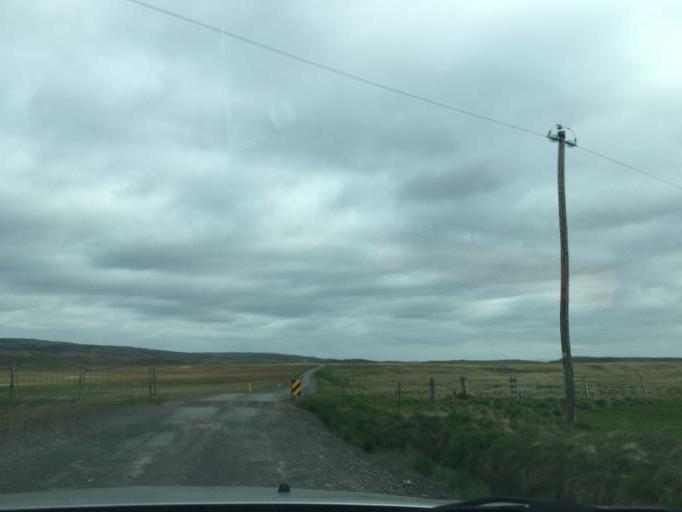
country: IS
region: South
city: Vestmannaeyjar
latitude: 64.2807
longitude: -20.2248
